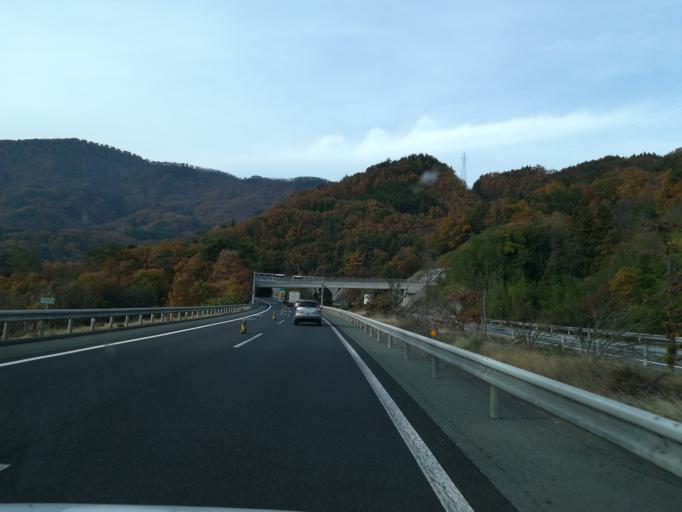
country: JP
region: Nagano
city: Ueda
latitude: 36.4720
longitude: 138.1972
